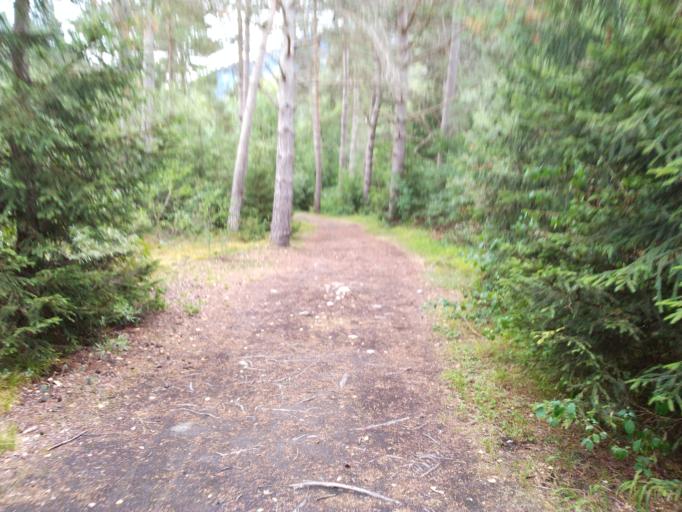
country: CH
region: Grisons
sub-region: Surselva District
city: Laax
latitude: 46.7848
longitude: 9.2447
